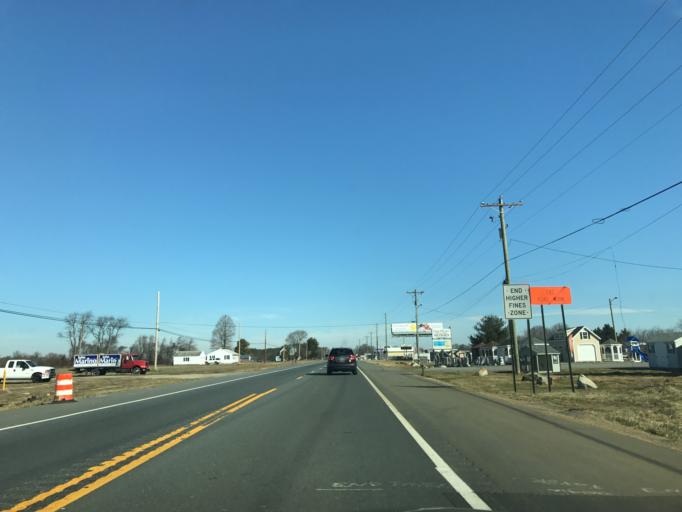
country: US
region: Delaware
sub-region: New Castle County
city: Middletown
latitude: 39.4899
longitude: -75.7168
